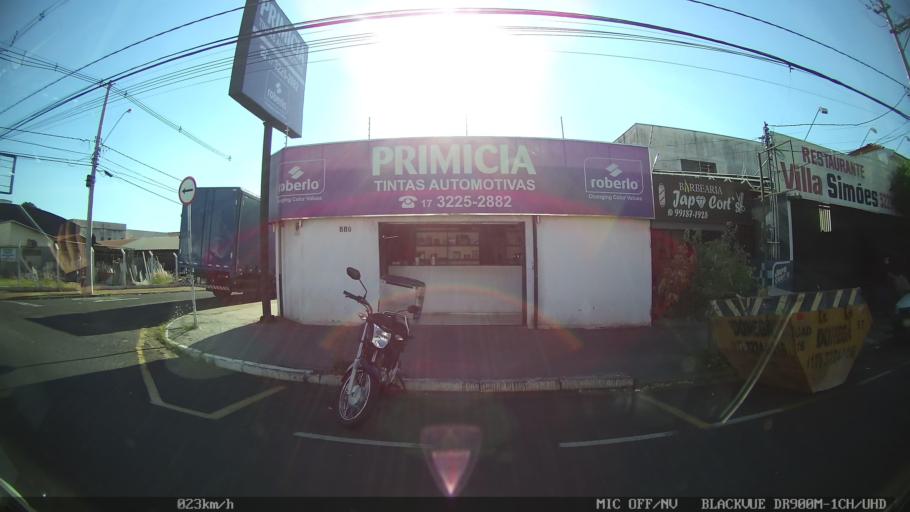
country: BR
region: Sao Paulo
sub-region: Sao Jose Do Rio Preto
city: Sao Jose do Rio Preto
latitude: -20.7898
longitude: -49.3595
